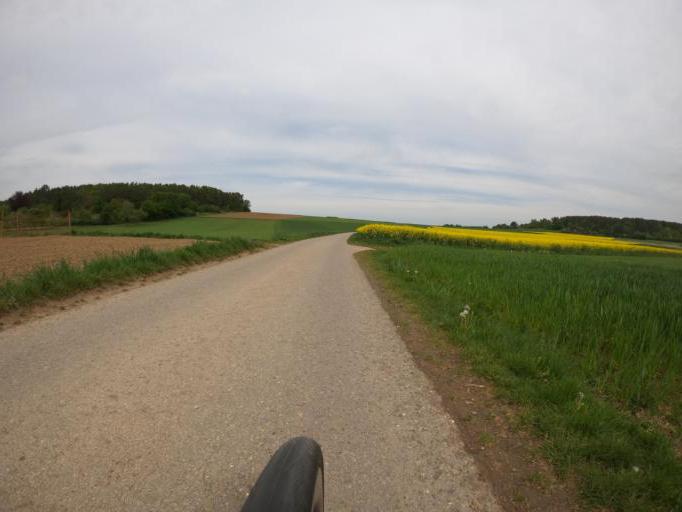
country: DE
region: Baden-Wuerttemberg
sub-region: Regierungsbezirk Stuttgart
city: Aidlingen
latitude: 48.6938
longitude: 8.8685
